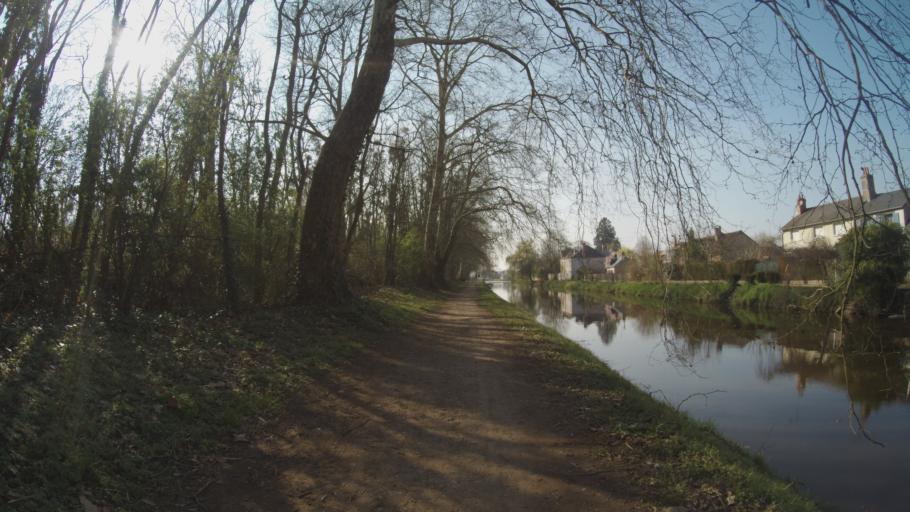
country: FR
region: Centre
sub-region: Departement du Loiret
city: Saint-Jean-de-Braye
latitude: 47.8977
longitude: 1.9926
